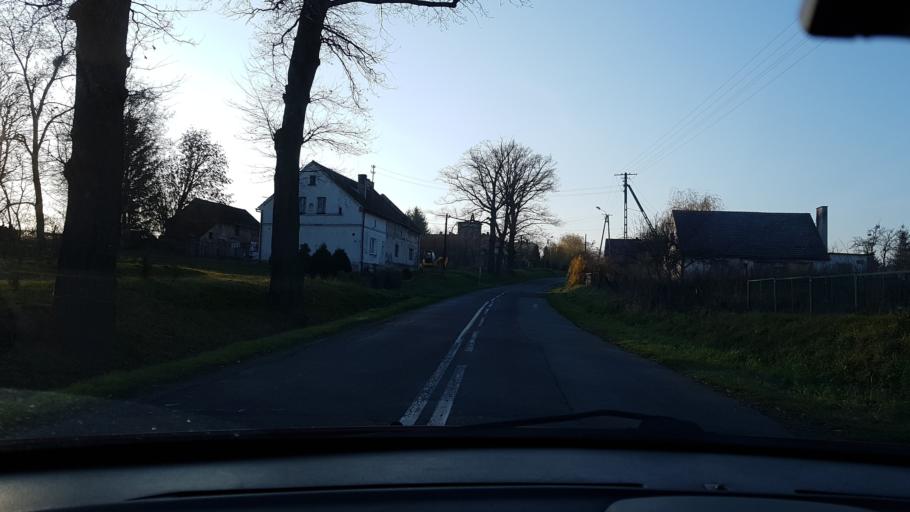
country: PL
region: Opole Voivodeship
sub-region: Powiat nyski
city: Chroscina
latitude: 50.6655
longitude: 17.2735
